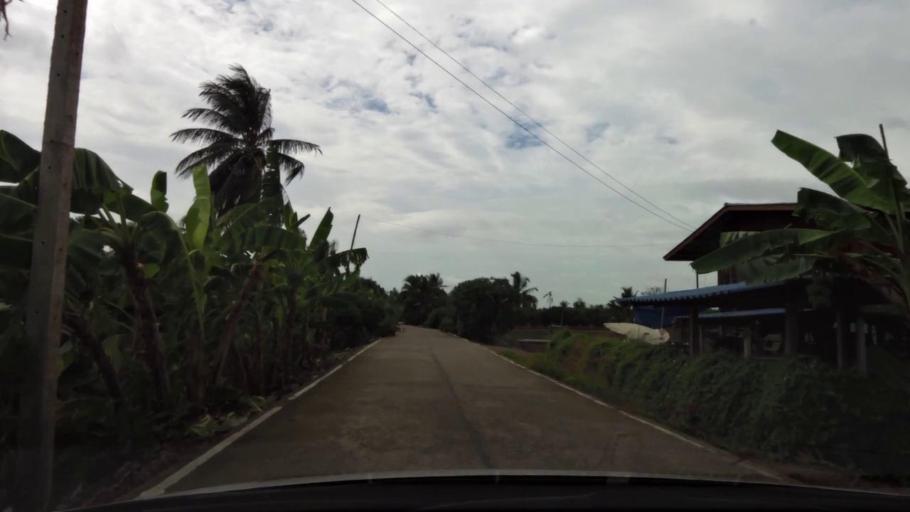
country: TH
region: Ratchaburi
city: Damnoen Saduak
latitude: 13.5480
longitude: 99.9865
